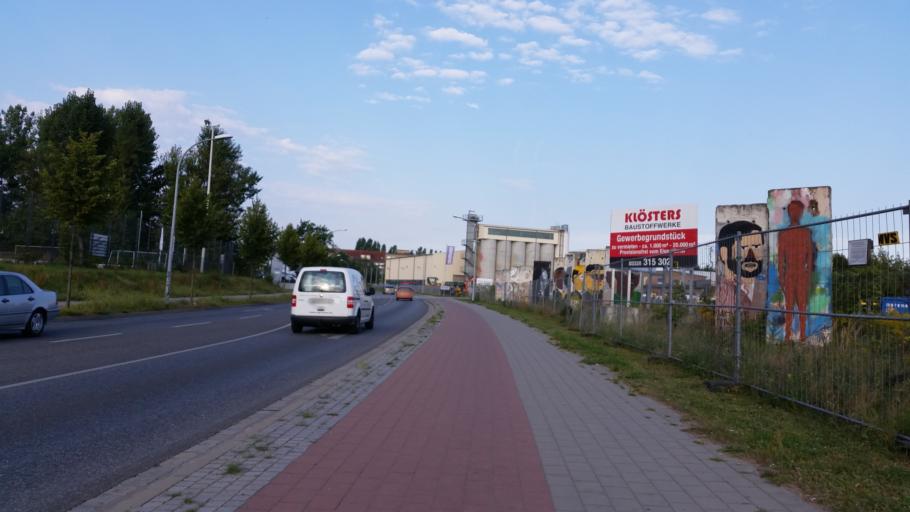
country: DE
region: Brandenburg
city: Teltow
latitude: 52.4049
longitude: 13.2588
